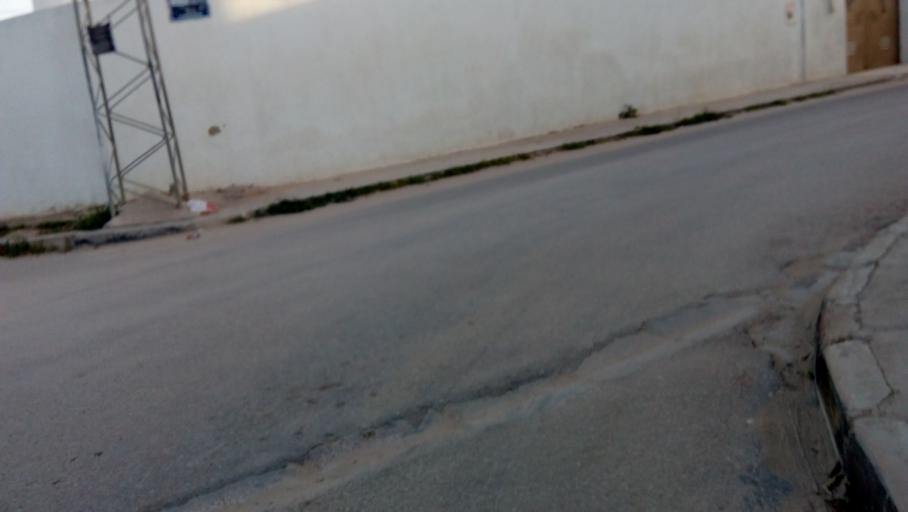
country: TN
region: Safaqis
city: Sfax
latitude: 34.7510
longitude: 10.7362
